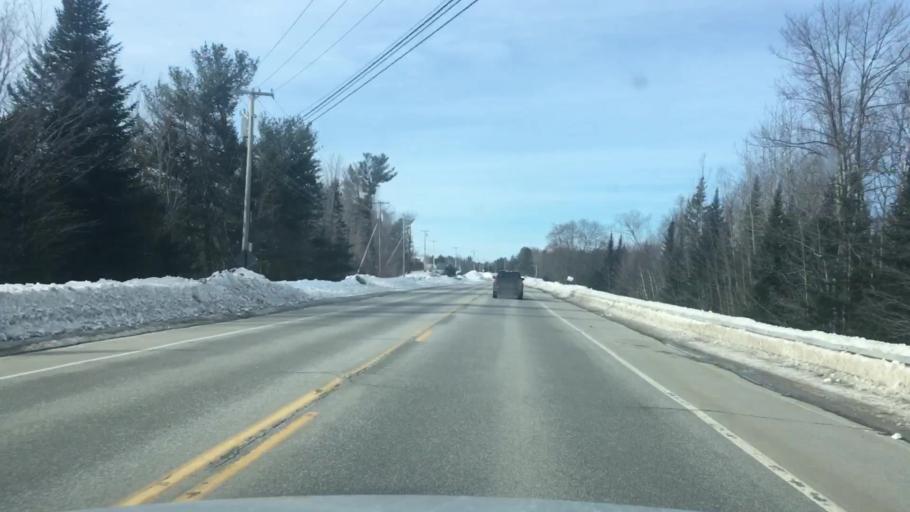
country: US
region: Maine
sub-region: Penobscot County
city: Kenduskeag
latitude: 44.9492
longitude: -68.9468
